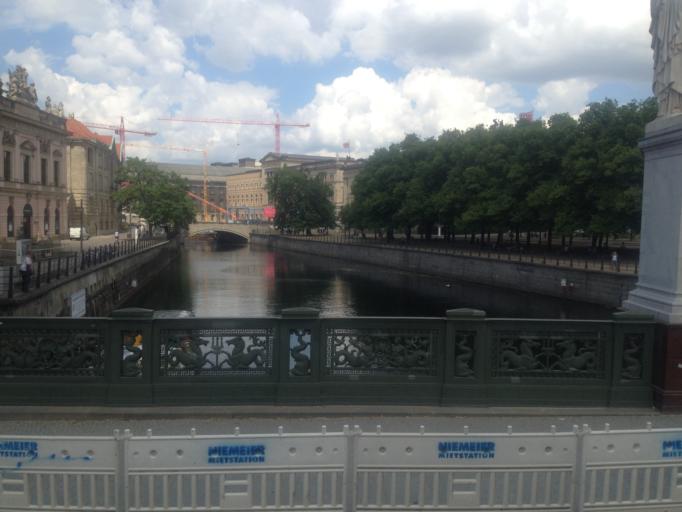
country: DE
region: Berlin
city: Mitte
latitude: 52.5177
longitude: 13.3983
